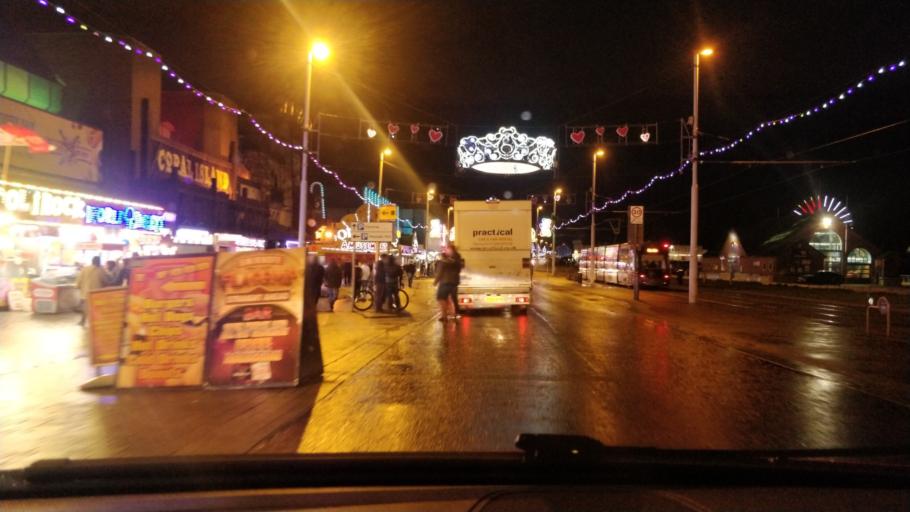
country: GB
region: England
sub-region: Blackpool
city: Blackpool
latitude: 53.8144
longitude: -3.0555
